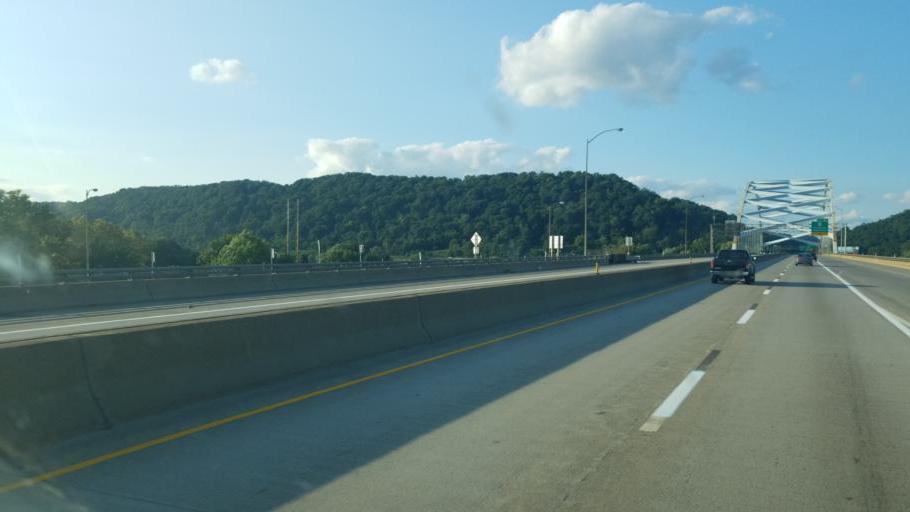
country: US
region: Pennsylvania
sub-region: Allegheny County
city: Coraopolis
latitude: 40.5119
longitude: -80.1352
